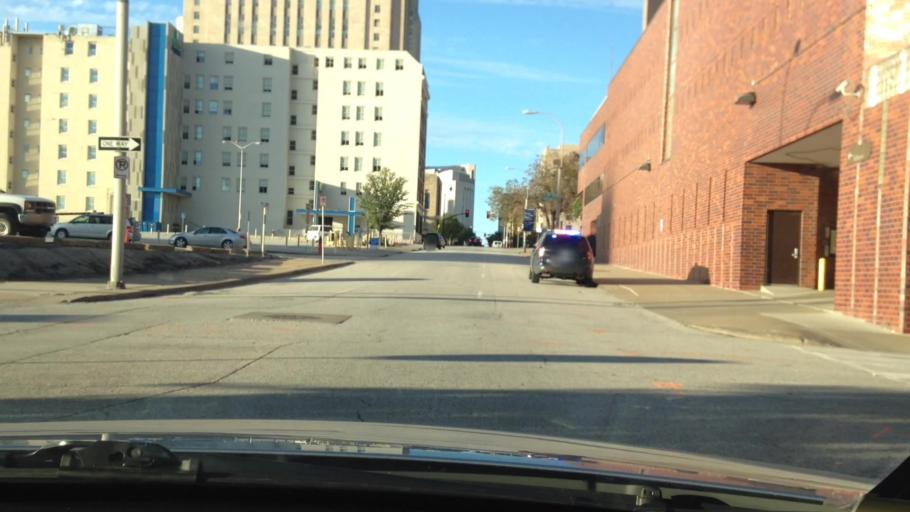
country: US
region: Missouri
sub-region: Jackson County
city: Kansas City
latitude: 39.0970
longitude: -94.5775
